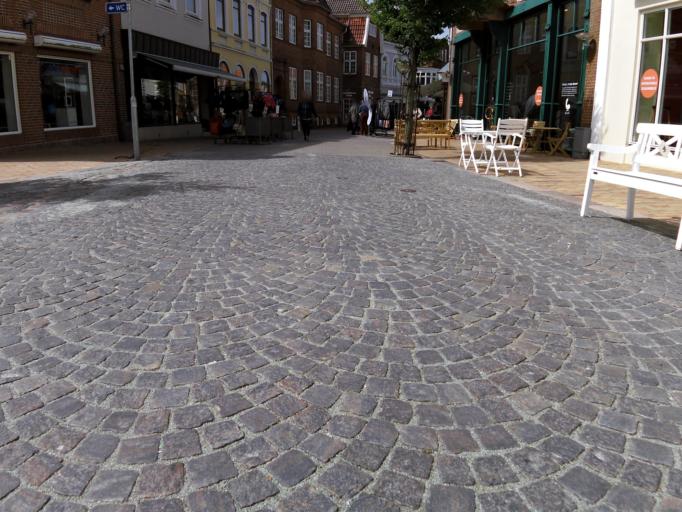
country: DK
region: South Denmark
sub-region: Tonder Kommune
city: Tonder
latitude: 54.9346
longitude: 8.8664
